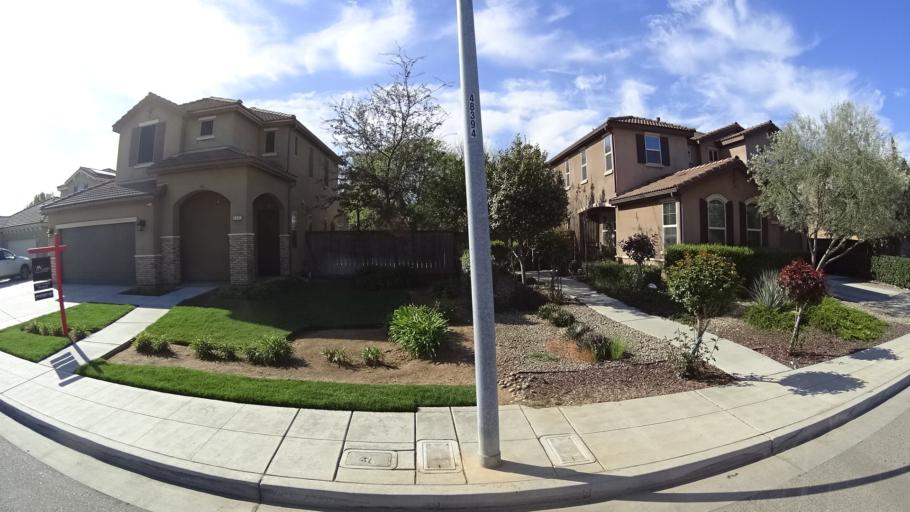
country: US
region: California
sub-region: Fresno County
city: West Park
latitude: 36.7971
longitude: -119.8950
